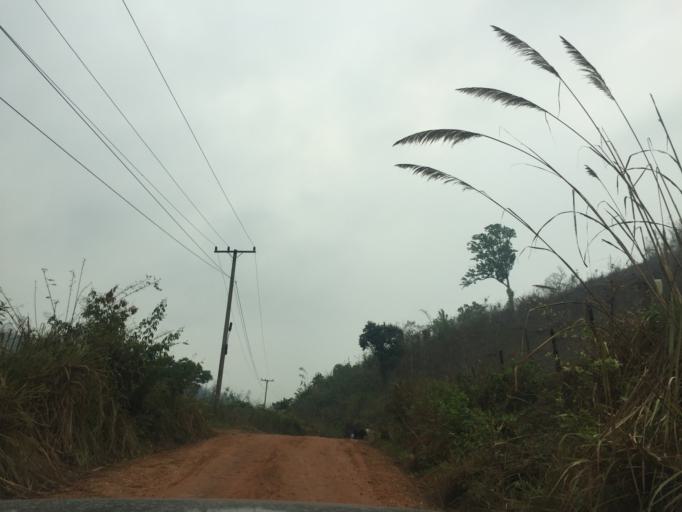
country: TH
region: Nan
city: Bo Kluea
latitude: 18.8613
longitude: 101.4316
